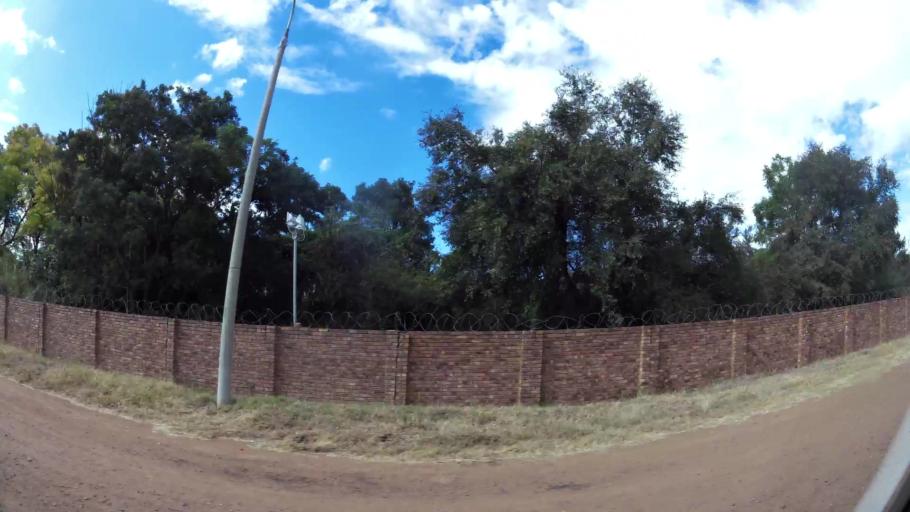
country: ZA
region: Limpopo
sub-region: Waterberg District Municipality
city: Warmbaths
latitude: -24.8902
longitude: 28.2837
